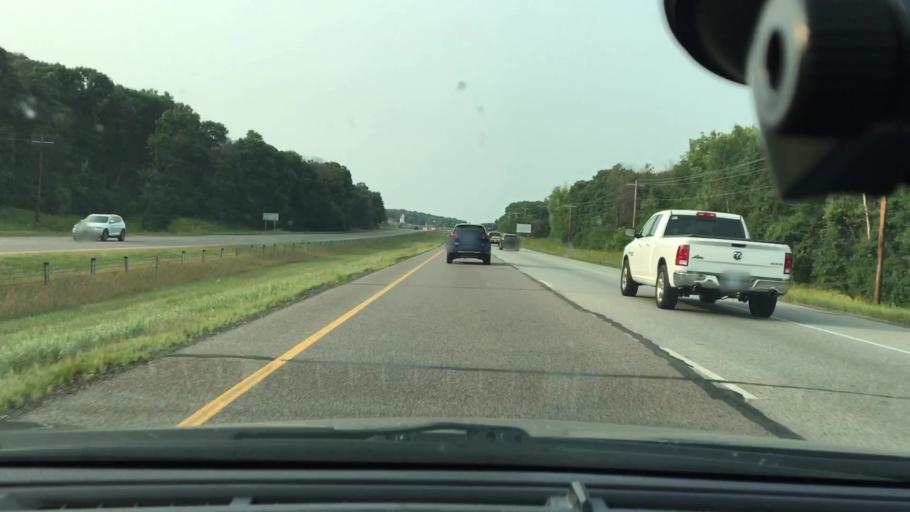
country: US
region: Minnesota
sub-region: Sherburne County
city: Elk River
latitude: 45.3322
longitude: -93.5607
